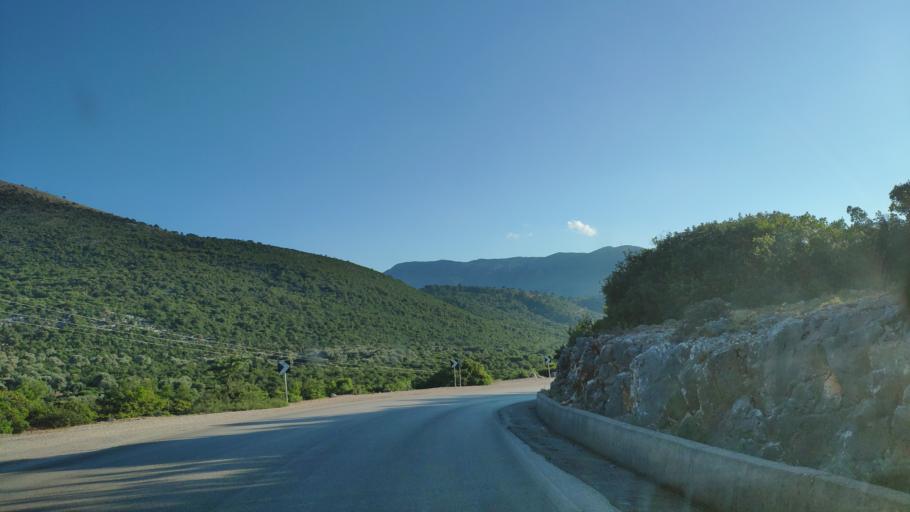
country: GR
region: West Greece
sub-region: Nomos Aitolias kai Akarnanias
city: Astakos
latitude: 38.6047
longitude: 21.1188
